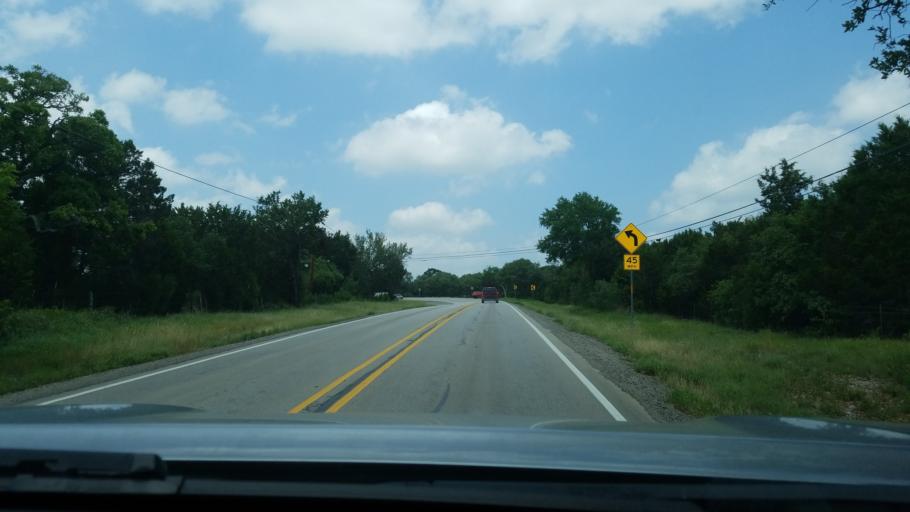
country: US
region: Texas
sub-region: Hays County
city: Dripping Springs
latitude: 30.1569
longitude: -98.0674
